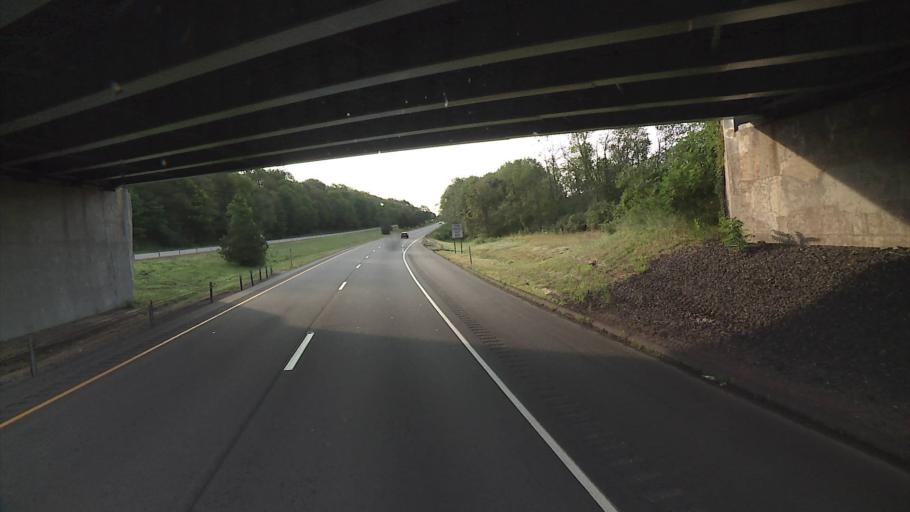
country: US
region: Connecticut
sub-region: New London County
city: Colchester
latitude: 41.5818
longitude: -72.3590
